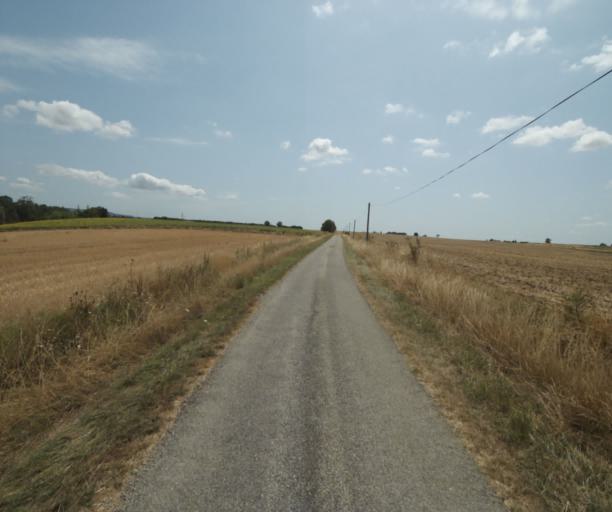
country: FR
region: Midi-Pyrenees
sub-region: Departement de la Haute-Garonne
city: Saint-Felix-Lauragais
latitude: 43.3977
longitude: 1.9001
